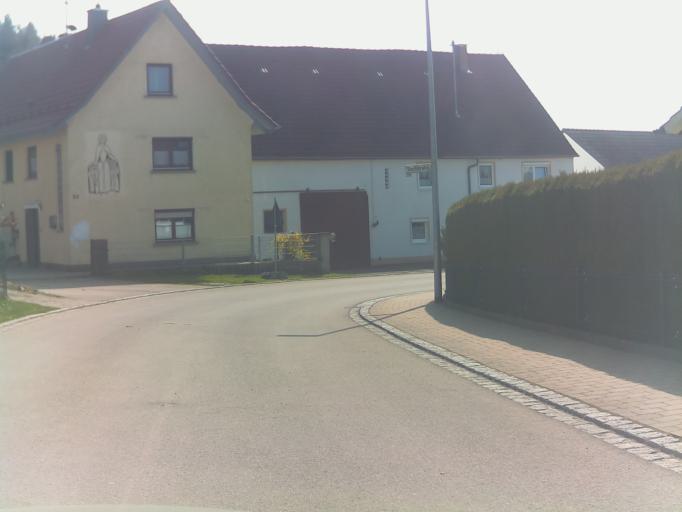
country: DE
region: Bavaria
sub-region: Swabia
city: Altenstadt
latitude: 48.1864
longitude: 10.1163
